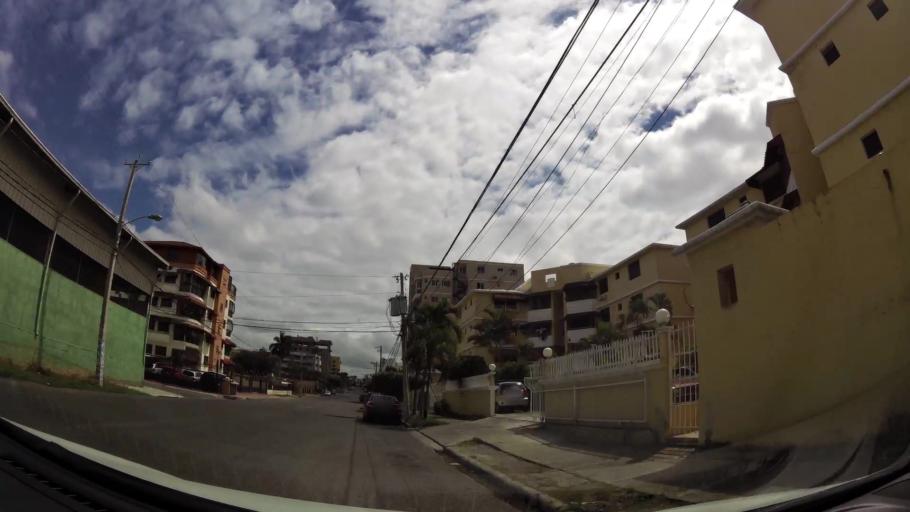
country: DO
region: Nacional
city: Bella Vista
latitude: 18.4719
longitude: -69.9565
